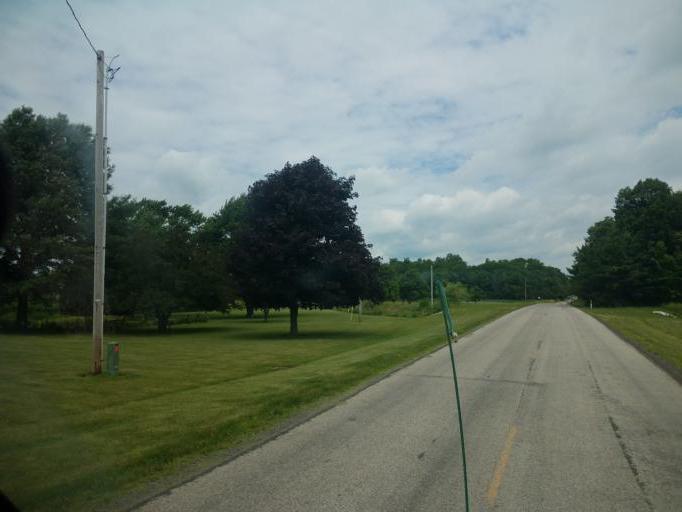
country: US
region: Ohio
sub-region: Crawford County
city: Crestline
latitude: 40.7970
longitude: -82.6978
